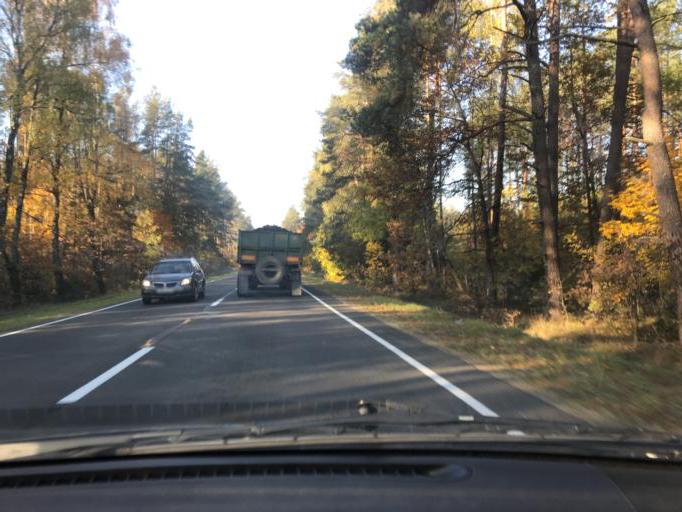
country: BY
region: Brest
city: Tsyelyakhany
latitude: 52.8694
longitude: 25.7105
